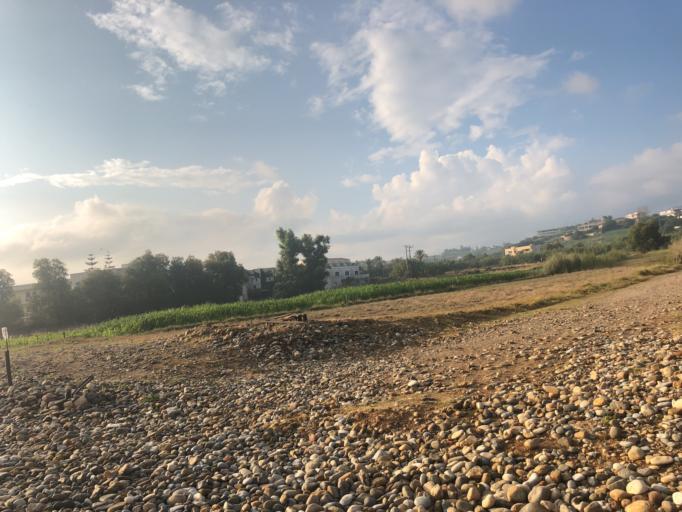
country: GR
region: Crete
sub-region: Nomos Chanias
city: Georgioupolis
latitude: 35.3530
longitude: 24.3086
